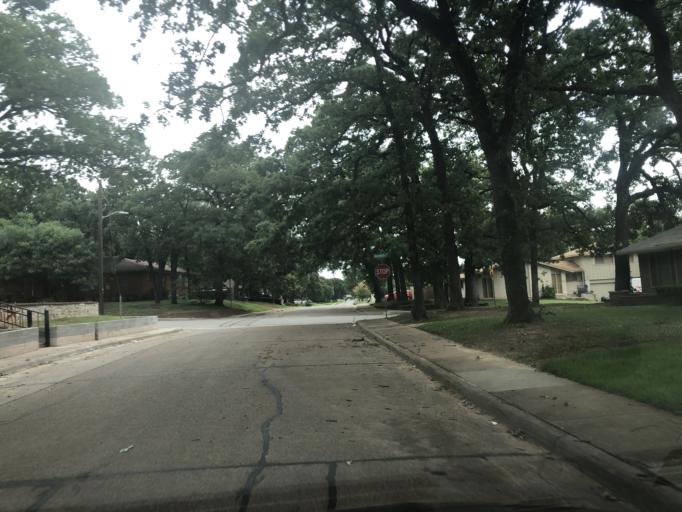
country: US
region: Texas
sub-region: Dallas County
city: Irving
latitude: 32.7983
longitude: -96.9744
